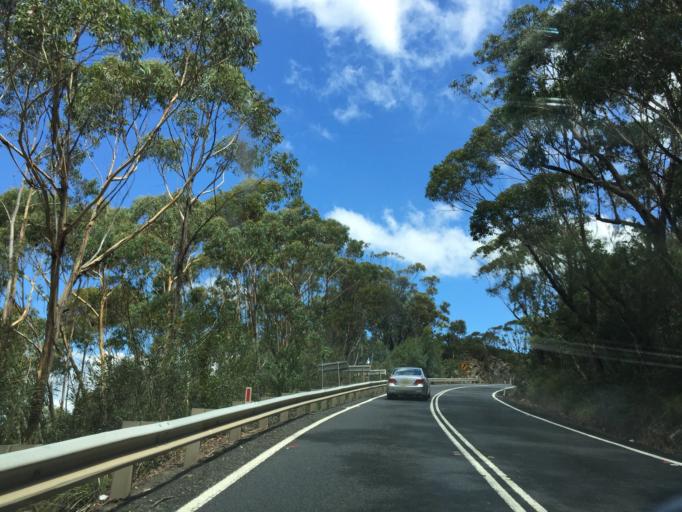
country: AU
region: New South Wales
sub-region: Blue Mountains Municipality
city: Blackheath
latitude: -33.5528
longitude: 150.3801
